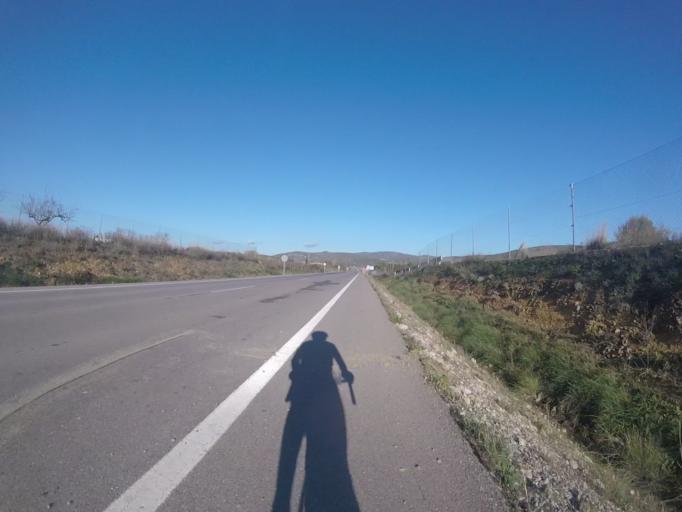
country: ES
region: Valencia
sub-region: Provincia de Castello
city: Cuevas de Vinroma
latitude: 40.3142
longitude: 0.1197
